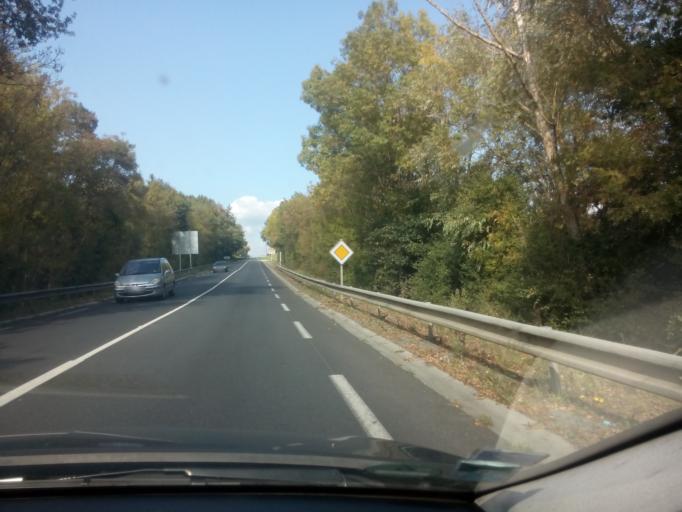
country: FR
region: Pays de la Loire
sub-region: Departement de Maine-et-Loire
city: Ecouflant
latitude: 47.5077
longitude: -0.5035
